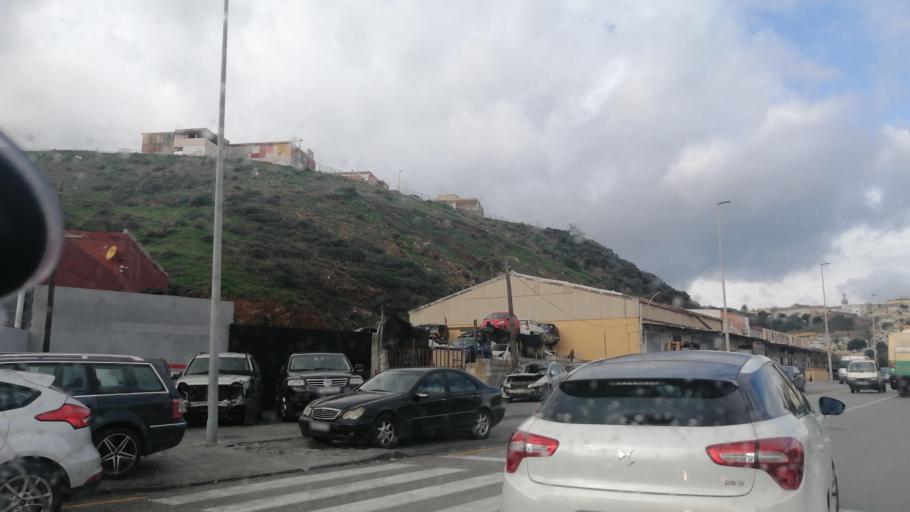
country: ES
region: Ceuta
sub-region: Ceuta
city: Ceuta
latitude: 35.8800
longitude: -5.3372
